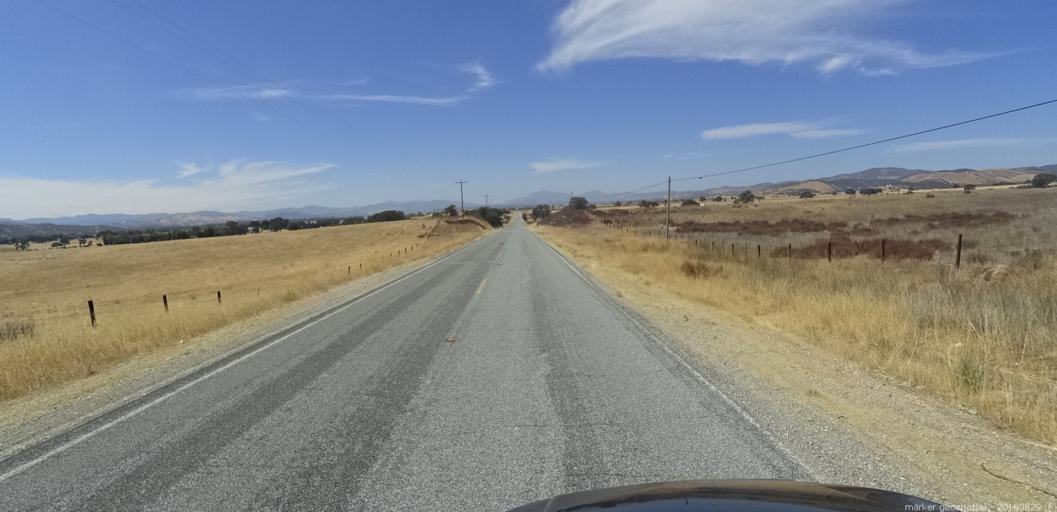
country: US
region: California
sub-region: San Luis Obispo County
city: Lake Nacimiento
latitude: 35.9273
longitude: -121.0464
